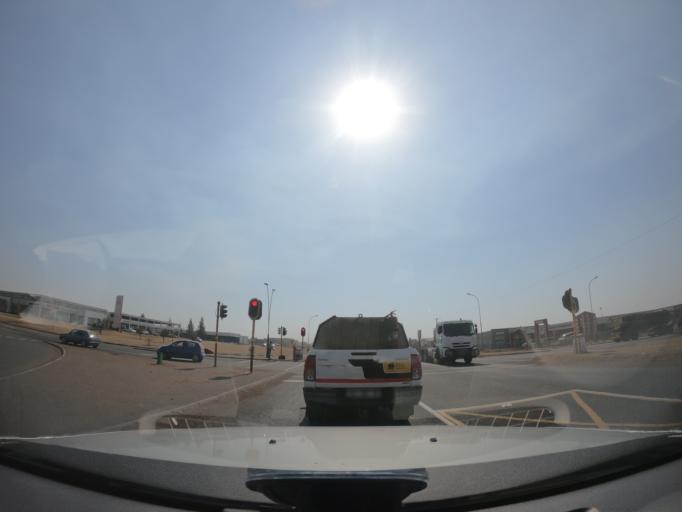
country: ZA
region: Mpumalanga
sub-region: Nkangala District Municipality
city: Middelburg
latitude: -25.8090
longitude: 29.4619
